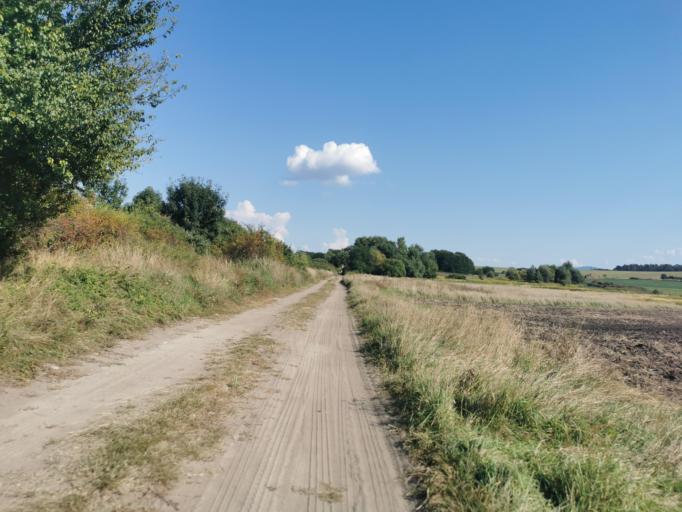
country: SK
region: Trnavsky
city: Gbely
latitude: 48.6224
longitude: 17.2261
